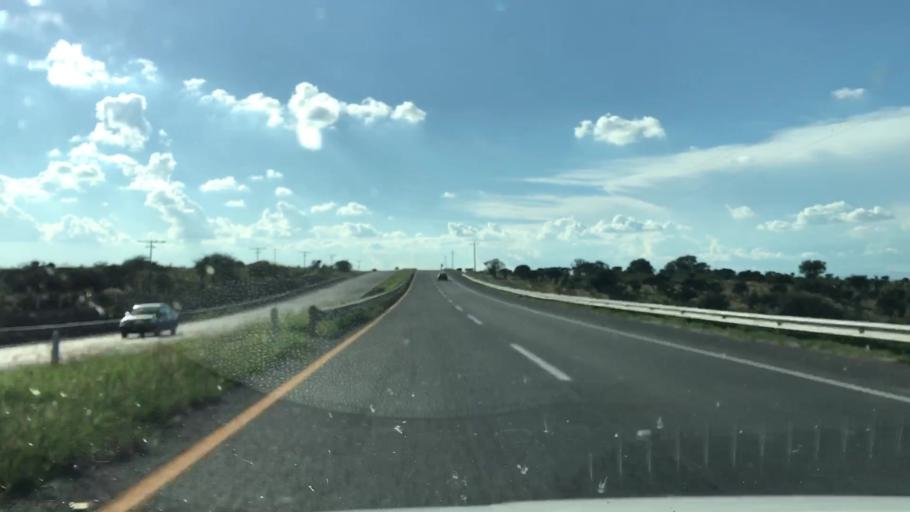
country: MX
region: Jalisco
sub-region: San Juan de los Lagos
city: Mezquitic de la Magdalena
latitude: 21.2895
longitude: -102.2118
